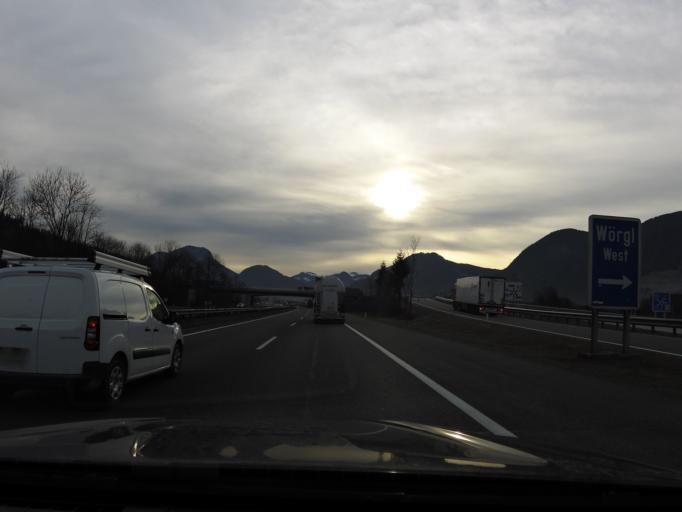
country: AT
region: Tyrol
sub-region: Politischer Bezirk Kufstein
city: Worgl
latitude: 47.4837
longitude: 12.0245
